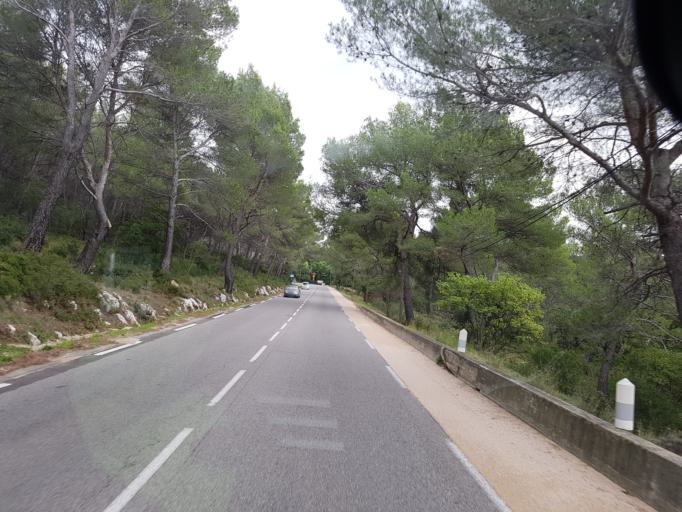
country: FR
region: Provence-Alpes-Cote d'Azur
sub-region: Departement des Bouches-du-Rhone
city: Cuges-les-Pins
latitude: 43.2687
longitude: 5.7188
